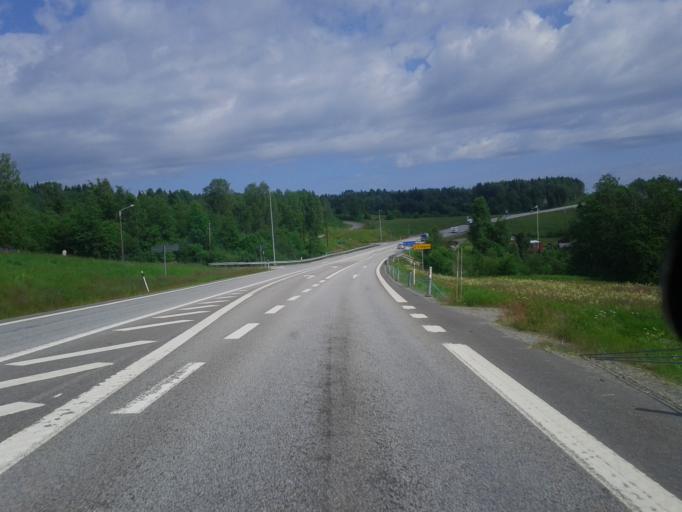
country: SE
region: Vaesternorrland
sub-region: OErnskoeldsviks Kommun
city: Ornskoldsvik
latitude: 63.3041
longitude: 18.9097
